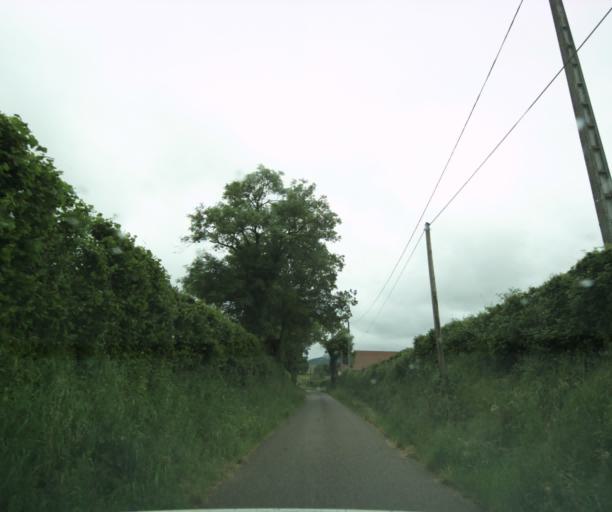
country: FR
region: Bourgogne
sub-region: Departement de Saone-et-Loire
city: Matour
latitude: 46.4371
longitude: 4.4446
